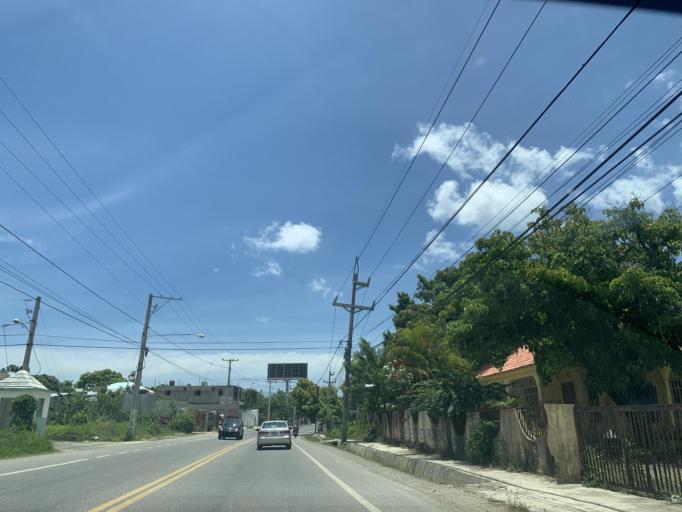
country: DO
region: Puerto Plata
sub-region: Puerto Plata
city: Puerto Plata
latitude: 19.7499
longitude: -70.5821
